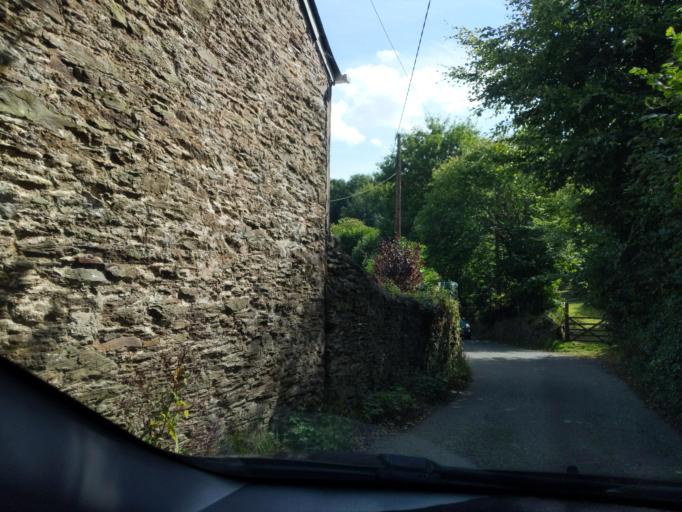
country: GB
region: England
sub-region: Cornwall
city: Torpoint
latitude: 50.3613
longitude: -4.2402
